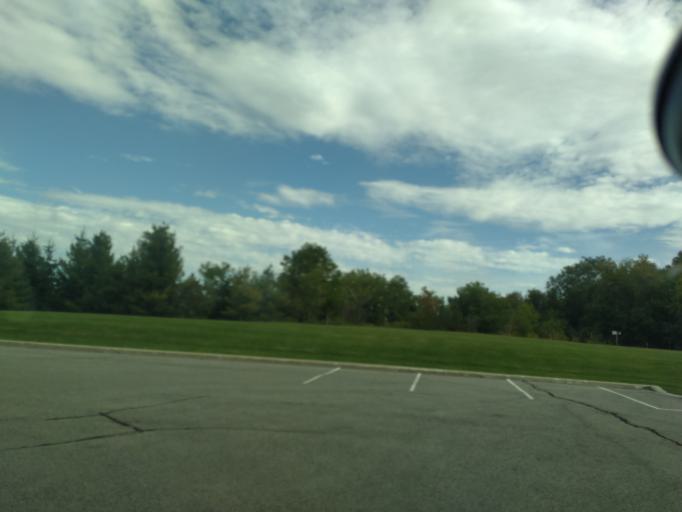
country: CA
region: Ontario
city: Newmarket
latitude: 44.0001
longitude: -79.4512
